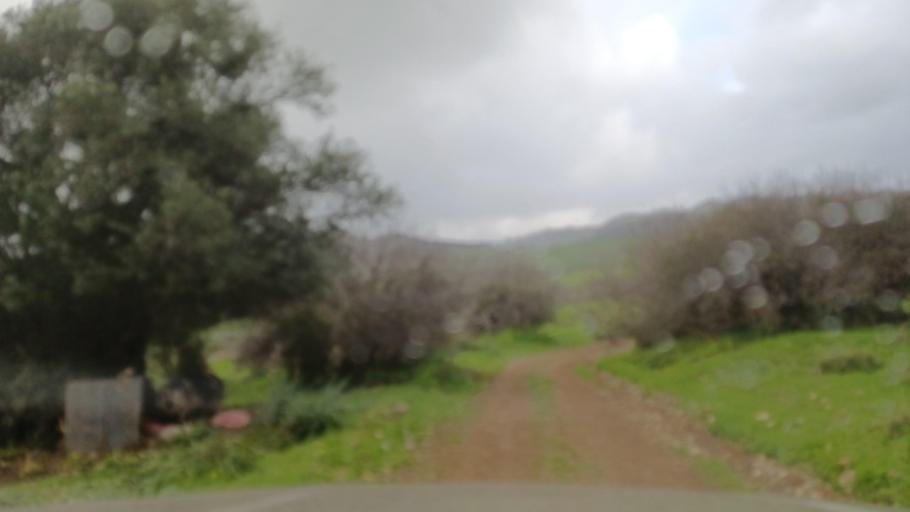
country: CY
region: Limassol
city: Pissouri
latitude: 34.7463
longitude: 32.6131
